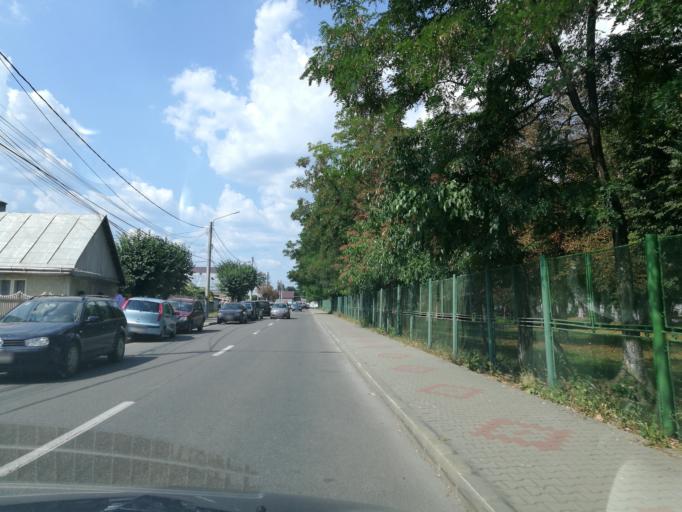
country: RO
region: Neamt
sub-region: Oras Targu Neamt
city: Humulesti
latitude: 47.2096
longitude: 26.3469
